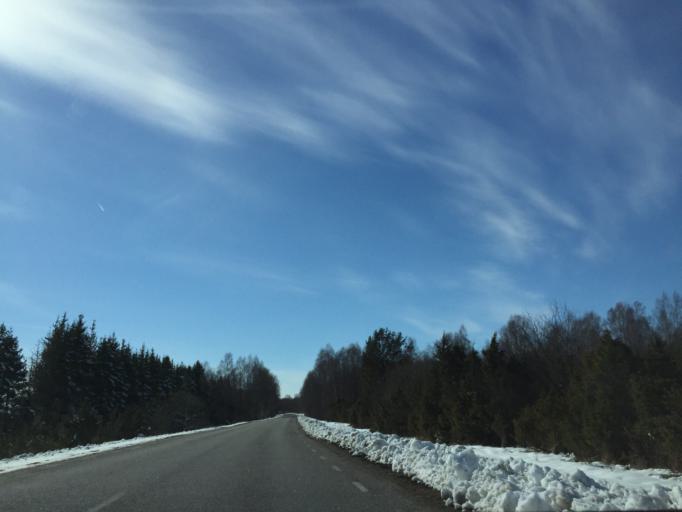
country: EE
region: Saare
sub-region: Orissaare vald
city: Orissaare
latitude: 58.4001
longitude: 22.9890
